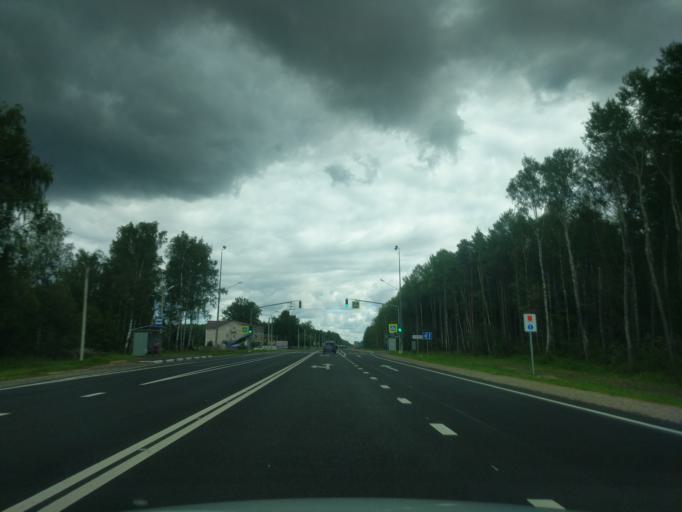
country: RU
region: Jaroslavl
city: Tunoshna
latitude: 57.5459
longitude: 40.1563
